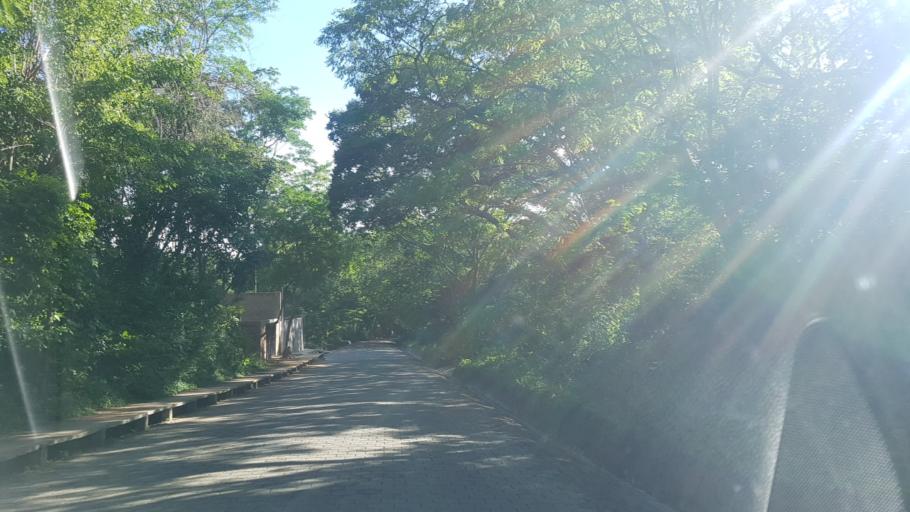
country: NI
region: Nueva Segovia
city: Mozonte
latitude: 13.6536
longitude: -86.4407
